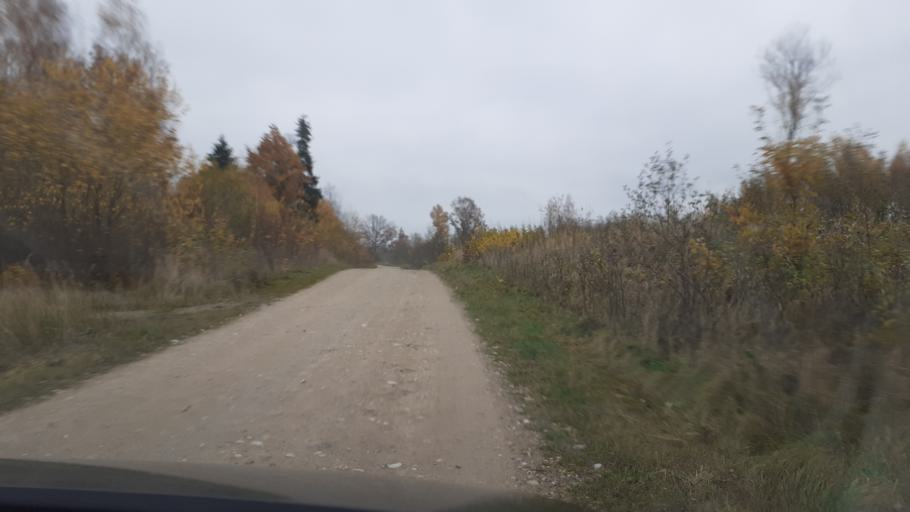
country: LV
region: Saldus Rajons
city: Saldus
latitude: 56.8612
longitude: 22.3332
